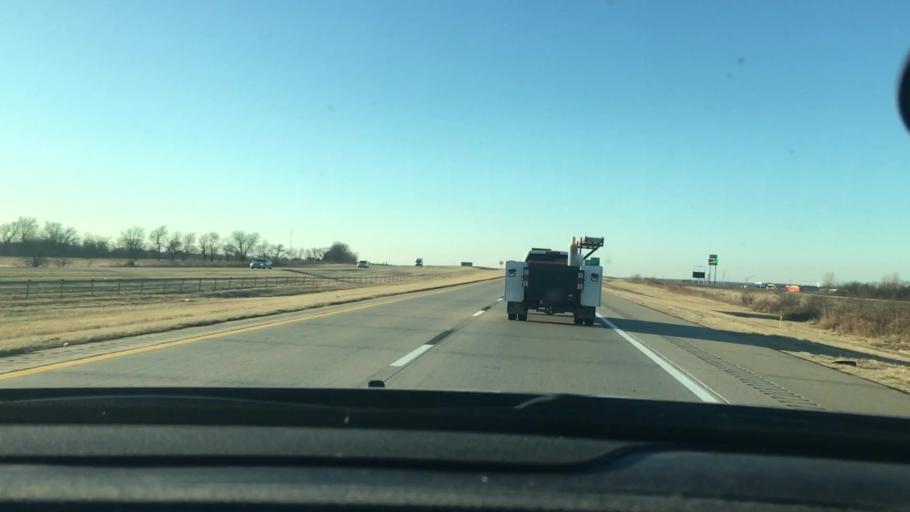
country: US
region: Oklahoma
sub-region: Carter County
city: Ardmore
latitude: 34.3388
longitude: -97.1501
